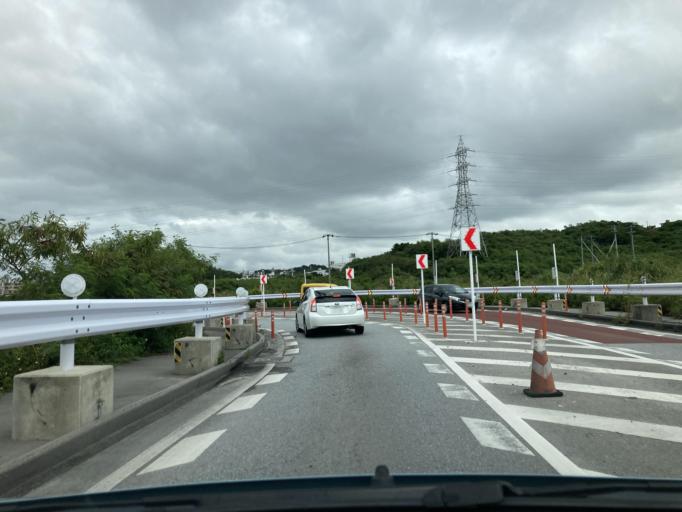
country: JP
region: Okinawa
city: Ginowan
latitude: 26.2399
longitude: 127.7451
